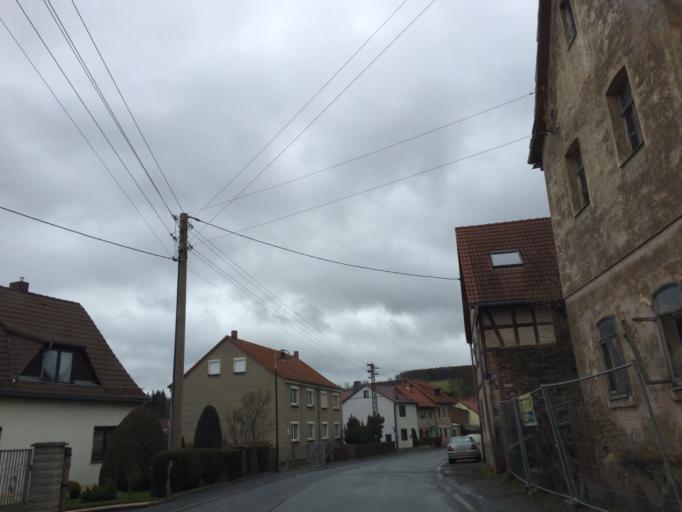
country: DE
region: Thuringia
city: Wernburg
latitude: 50.6765
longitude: 11.6052
